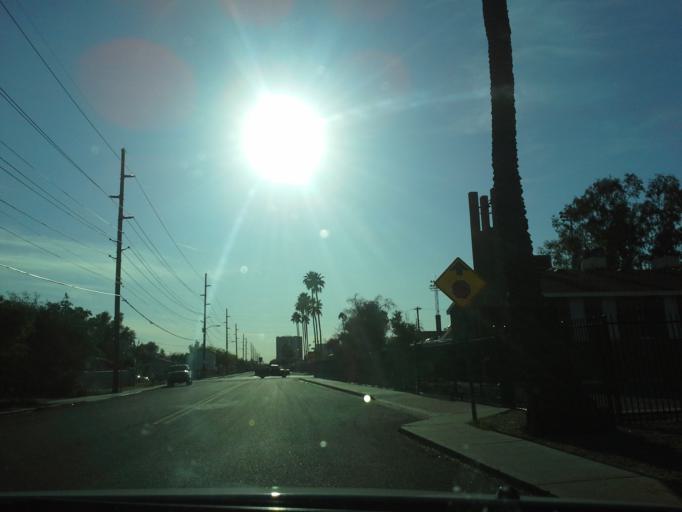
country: US
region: Arizona
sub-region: Maricopa County
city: Phoenix
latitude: 33.4765
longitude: -112.0553
